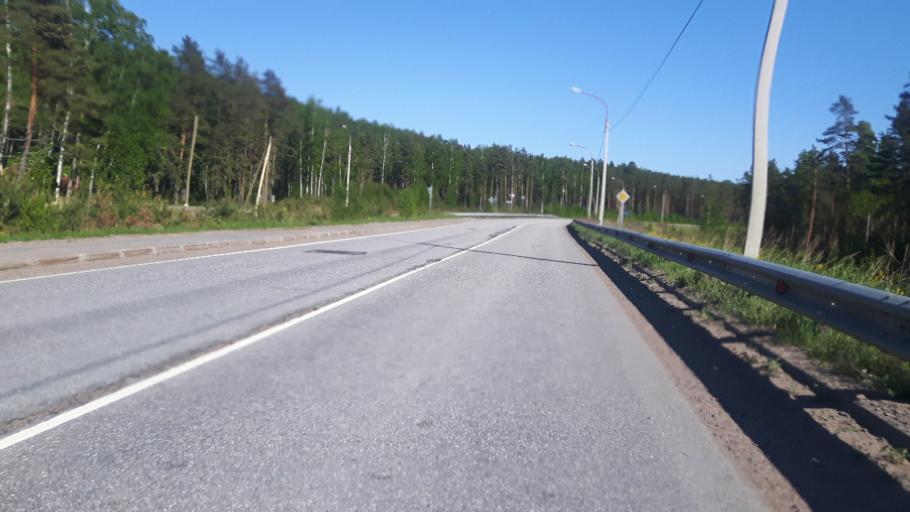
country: RU
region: Leningrad
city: Sosnovyy Bor
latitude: 60.1897
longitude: 29.0178
